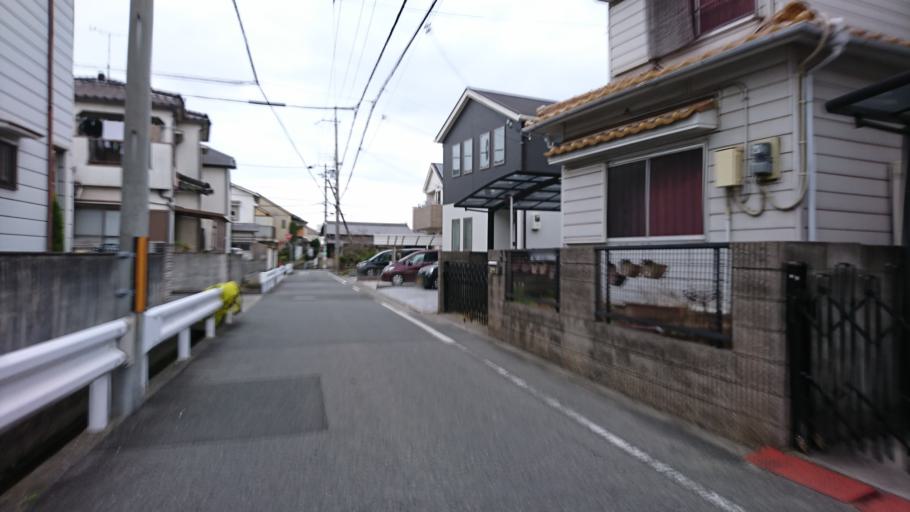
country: JP
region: Hyogo
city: Kakogawacho-honmachi
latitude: 34.7413
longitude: 134.8470
